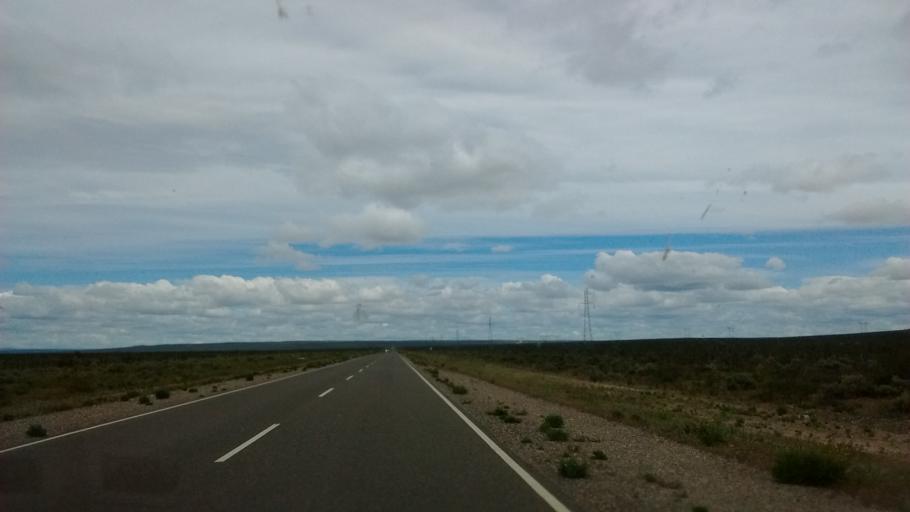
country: AR
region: Neuquen
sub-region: Departamento de Picun Leufu
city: Picun Leufu
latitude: -39.6864
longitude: -69.4703
